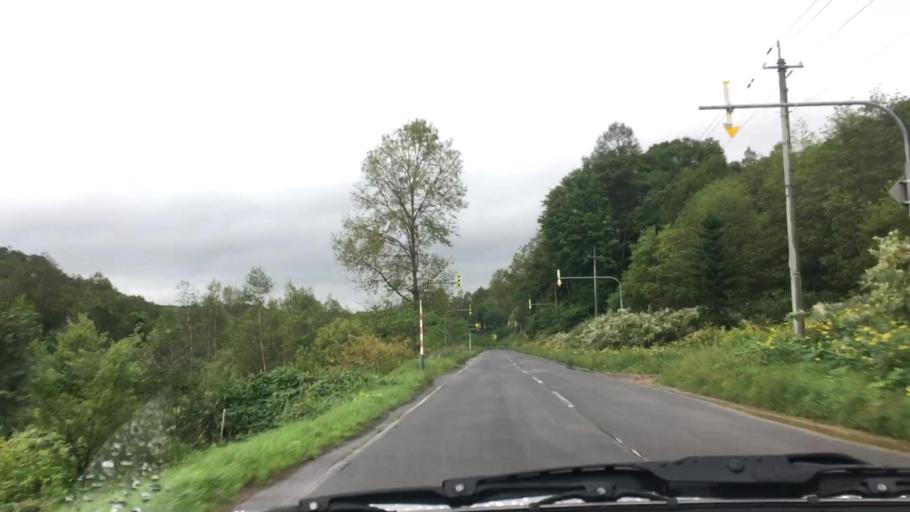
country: JP
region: Hokkaido
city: Niseko Town
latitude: 42.6625
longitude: 140.7754
